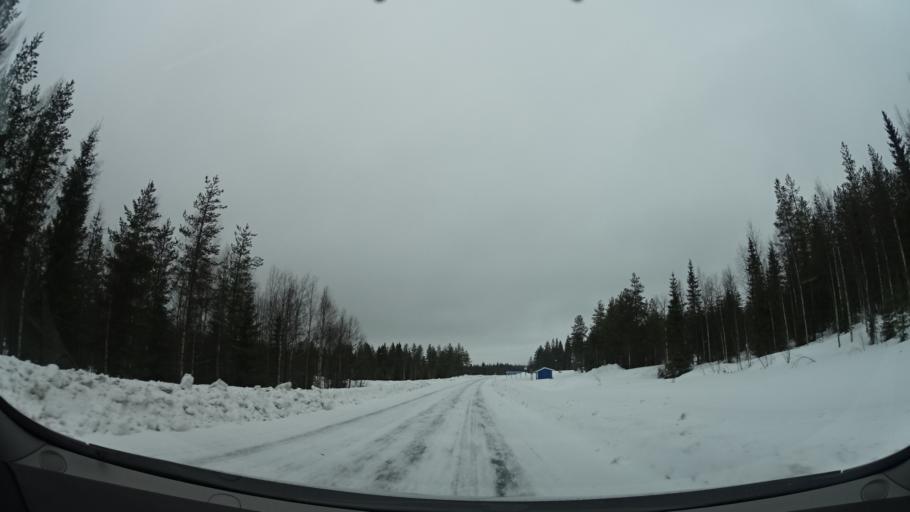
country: SE
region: Vaesterbotten
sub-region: Mala Kommun
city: Mala
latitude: 65.1056
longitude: 18.8932
